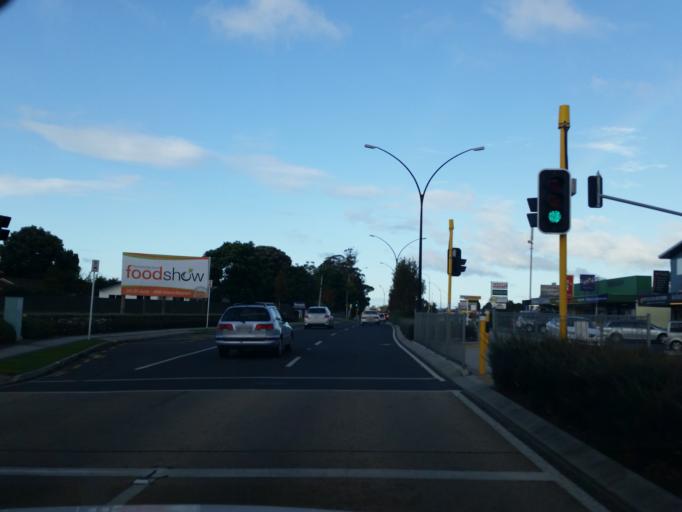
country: NZ
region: Bay of Plenty
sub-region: Tauranga City
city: Tauranga
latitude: -37.6956
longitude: 176.1090
